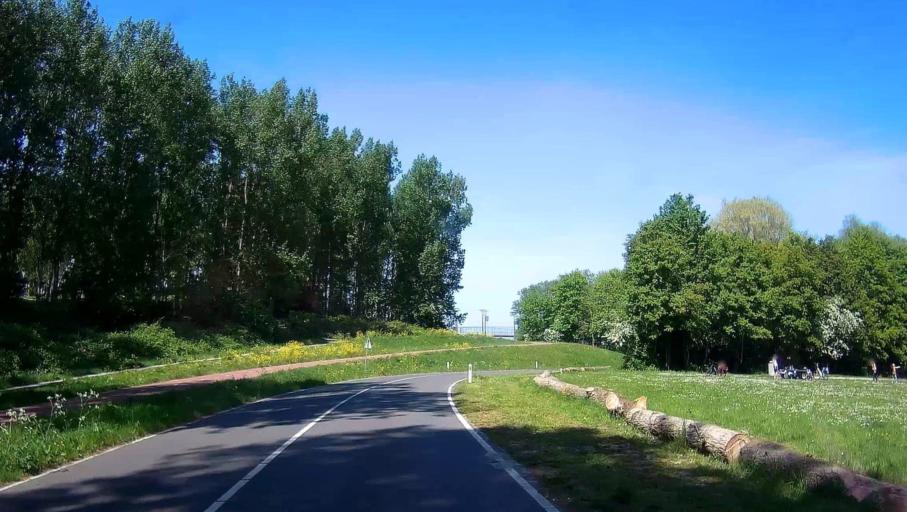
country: NL
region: South Holland
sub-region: Gemeente Pijnacker-Nootdorp
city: Pijnacker
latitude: 52.0560
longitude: 4.4381
